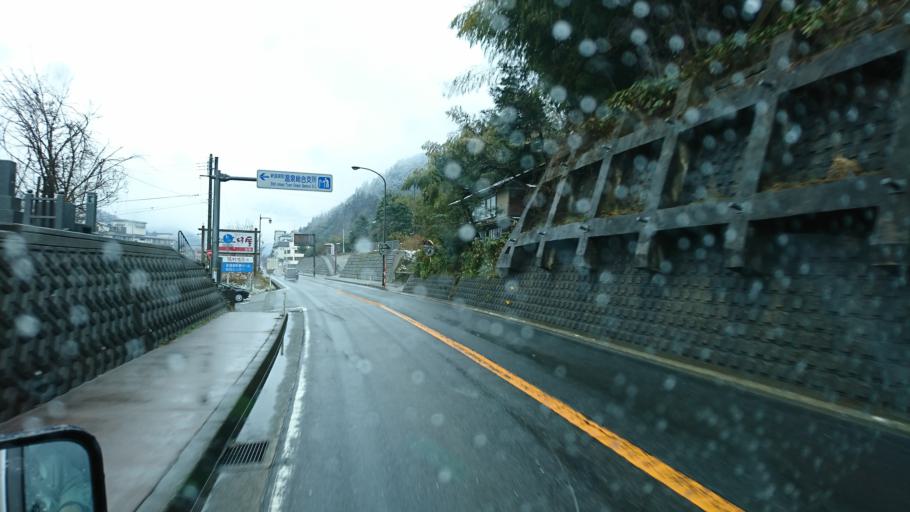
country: JP
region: Tottori
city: Tottori
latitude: 35.5537
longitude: 134.4922
